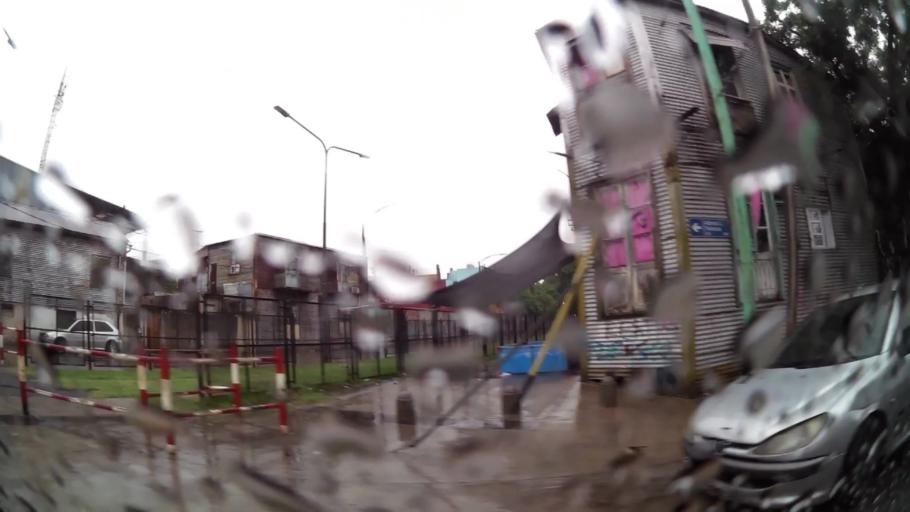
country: AR
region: Buenos Aires
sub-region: Partido de Avellaneda
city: Avellaneda
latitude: -34.6424
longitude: -58.3622
